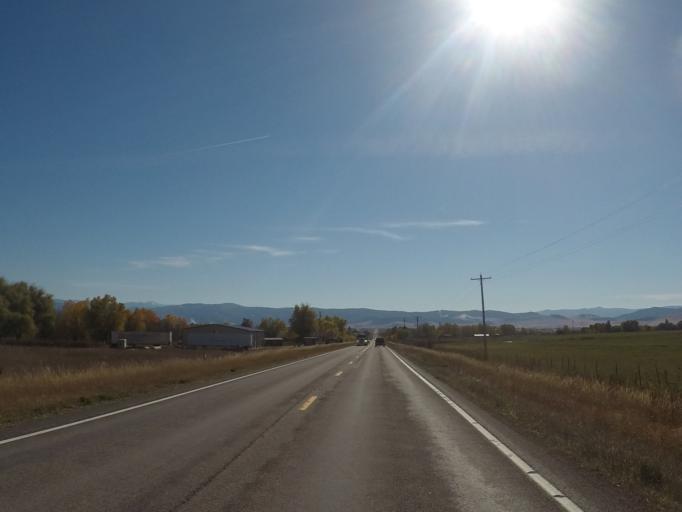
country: US
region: Montana
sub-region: Lake County
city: Ronan
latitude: 47.4018
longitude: -114.0969
